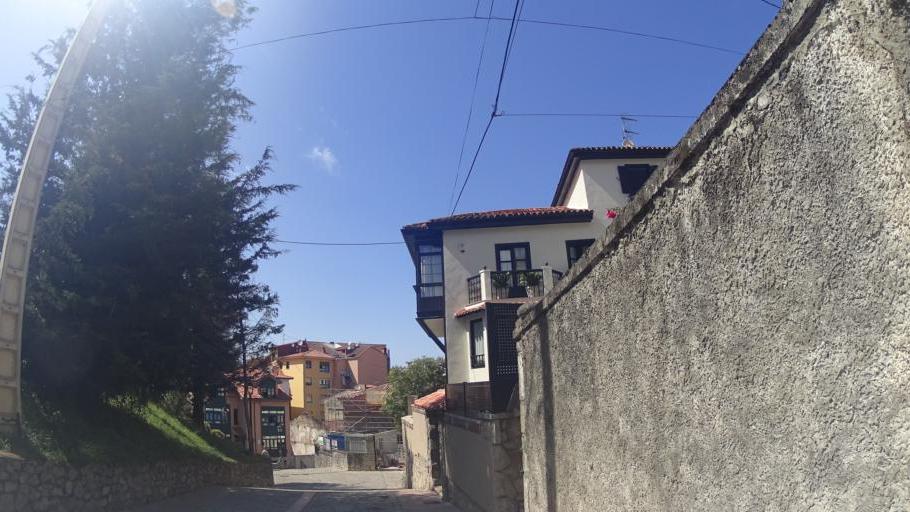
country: ES
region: Asturias
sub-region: Province of Asturias
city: Ribadesella
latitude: 43.4602
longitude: -5.0594
